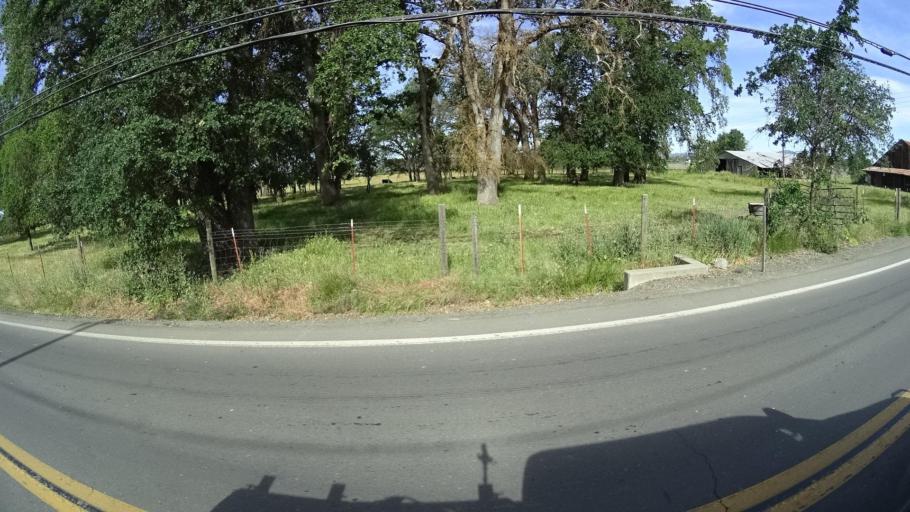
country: US
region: California
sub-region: Lake County
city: Kelseyville
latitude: 38.9888
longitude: -122.8291
